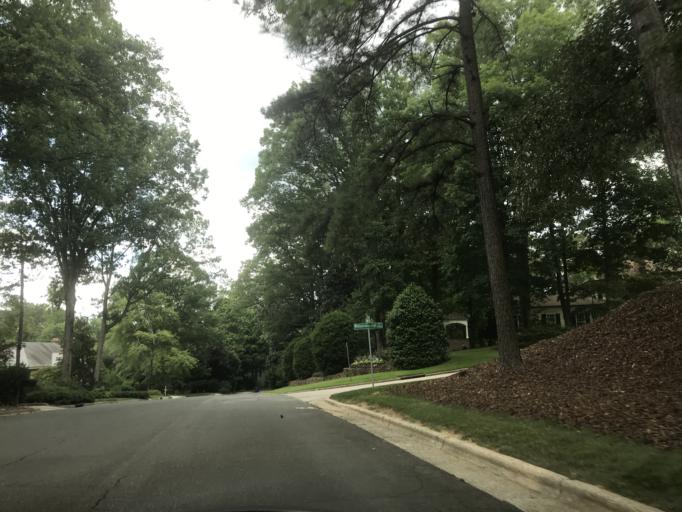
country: US
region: North Carolina
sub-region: Wake County
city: West Raleigh
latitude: 35.8292
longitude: -78.6517
